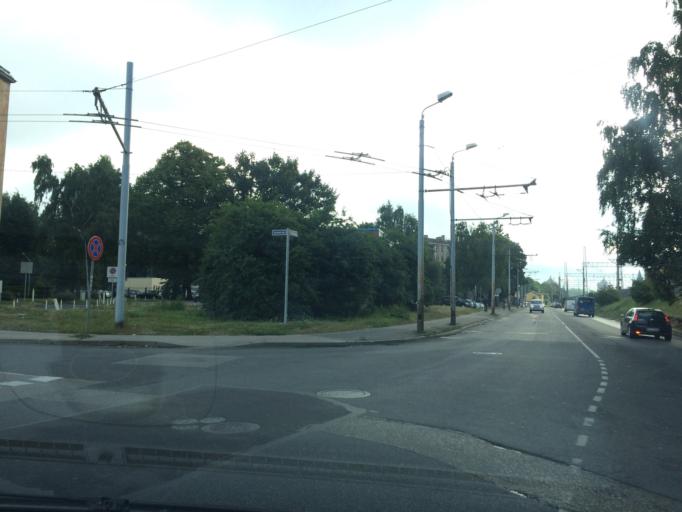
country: LV
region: Riga
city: Riga
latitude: 56.9471
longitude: 24.1371
